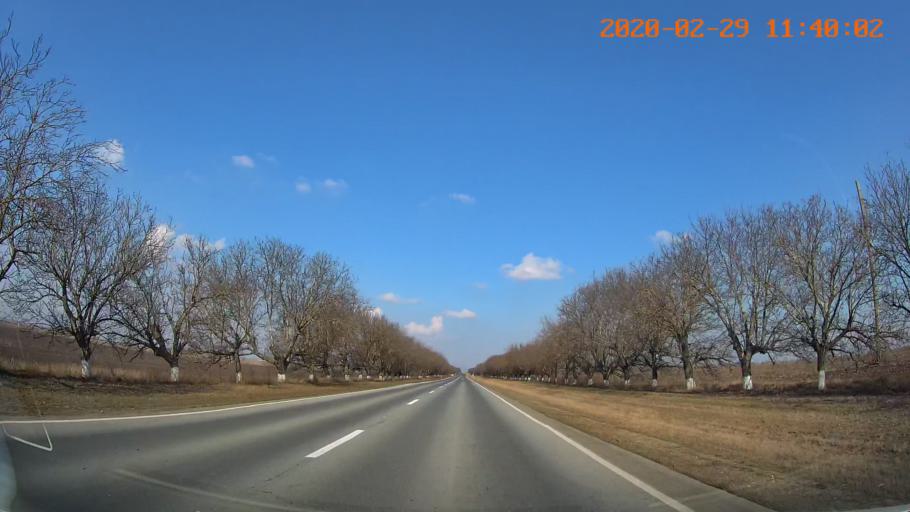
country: MD
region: Rezina
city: Saharna
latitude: 47.6497
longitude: 29.0219
